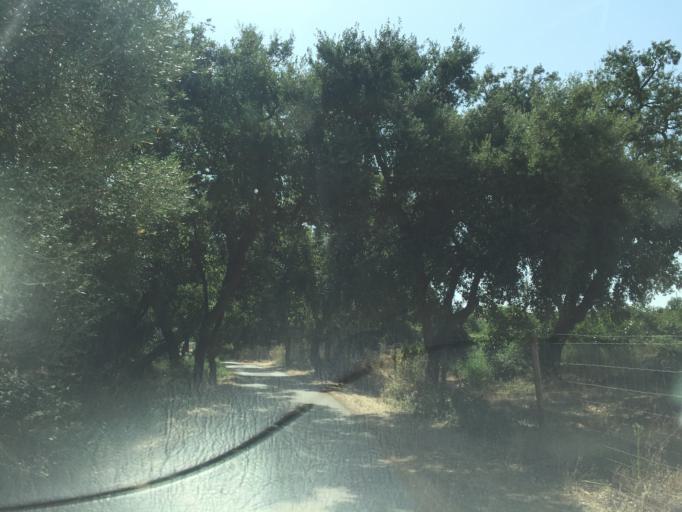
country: PT
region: Faro
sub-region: Loule
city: Boliqueime
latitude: 37.1090
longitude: -8.1929
